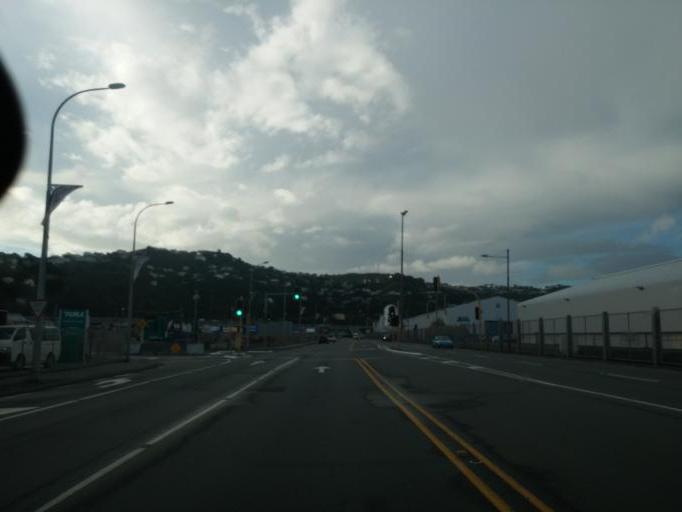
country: NZ
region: Wellington
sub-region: Wellington City
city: Wellington
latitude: -41.2709
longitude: 174.7865
